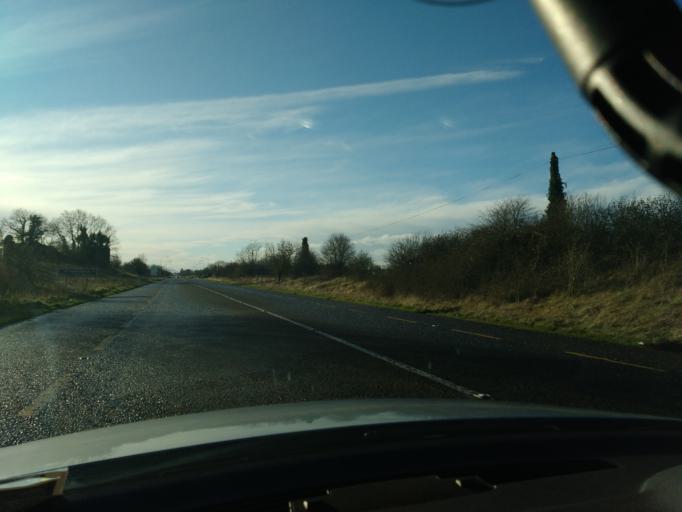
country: IE
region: Munster
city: Thurles
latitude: 52.6724
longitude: -7.6789
